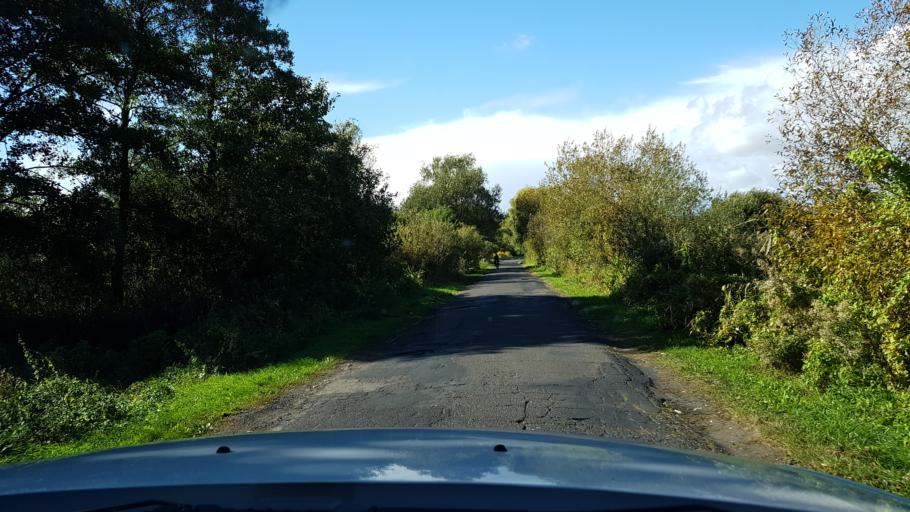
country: PL
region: West Pomeranian Voivodeship
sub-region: Powiat gryfinski
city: Gryfino
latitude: 53.2741
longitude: 14.4963
